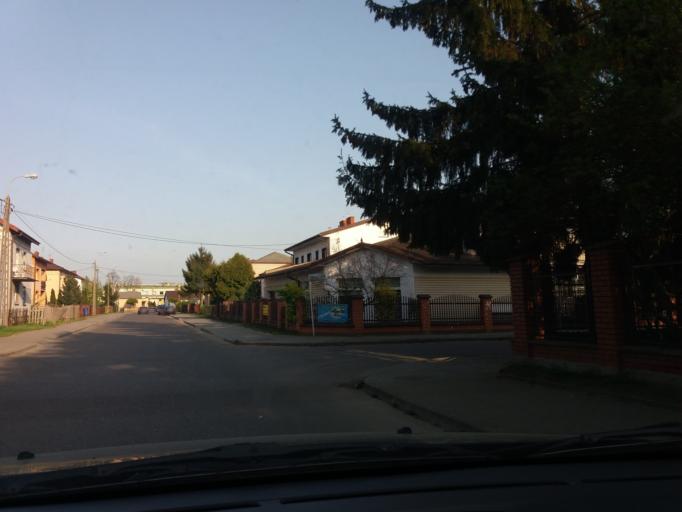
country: PL
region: Masovian Voivodeship
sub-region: Powiat mlawski
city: Mlawa
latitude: 53.1234
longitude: 20.3752
